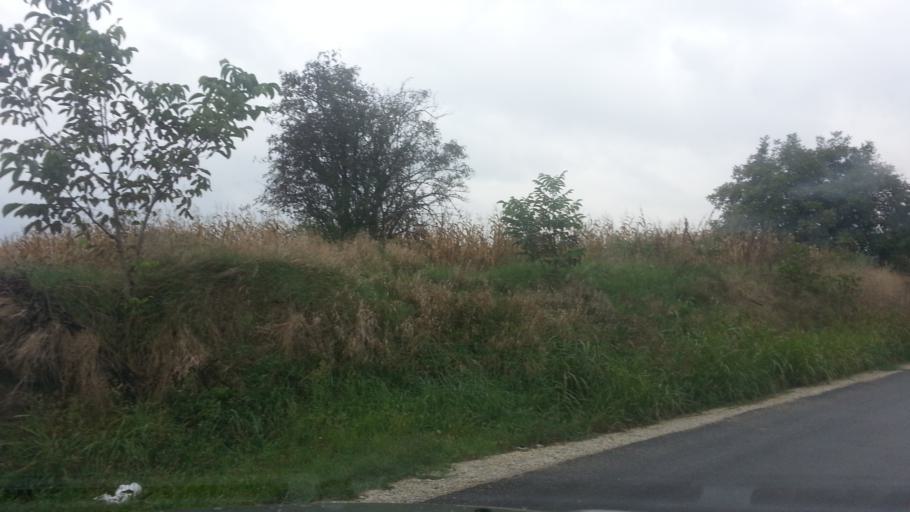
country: RS
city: Novi Banovci
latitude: 44.9385
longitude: 20.2959
